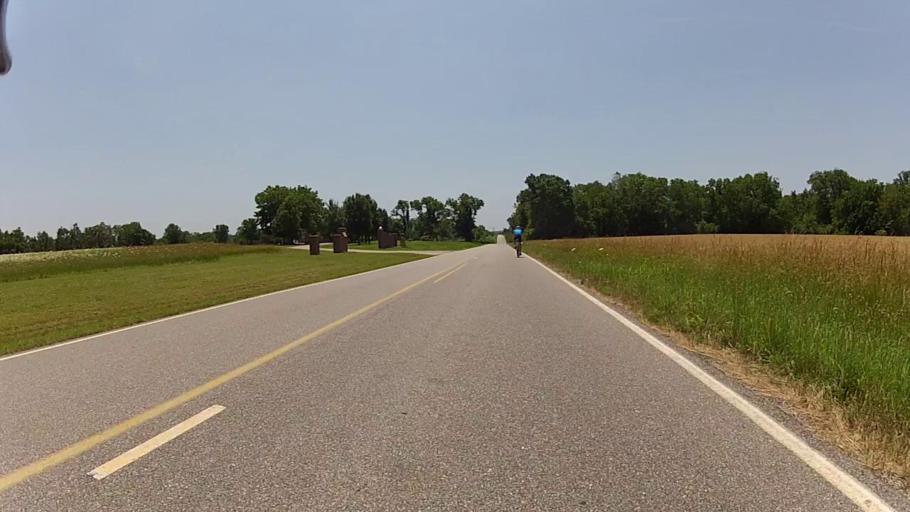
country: US
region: Kansas
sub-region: Montgomery County
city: Cherryvale
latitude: 37.2429
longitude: -95.5375
